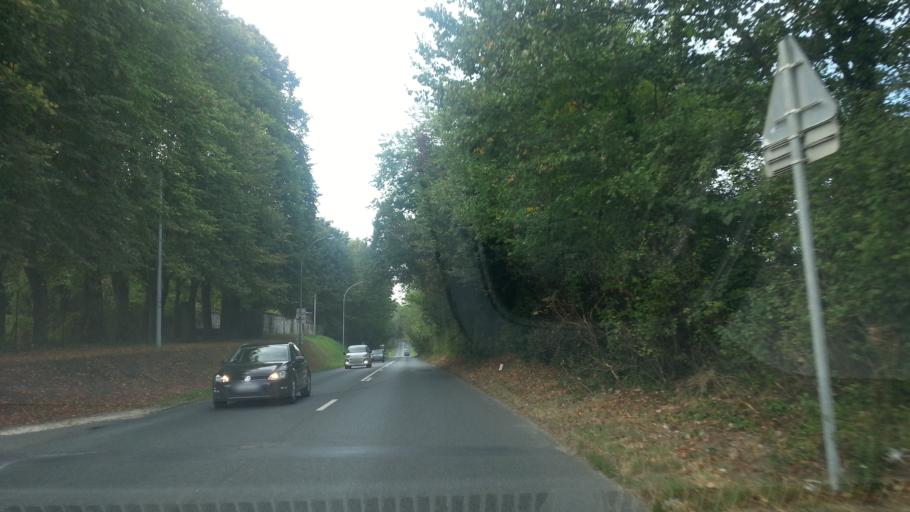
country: FR
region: Picardie
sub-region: Departement de l'Oise
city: Senlis
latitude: 49.2082
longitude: 2.5706
